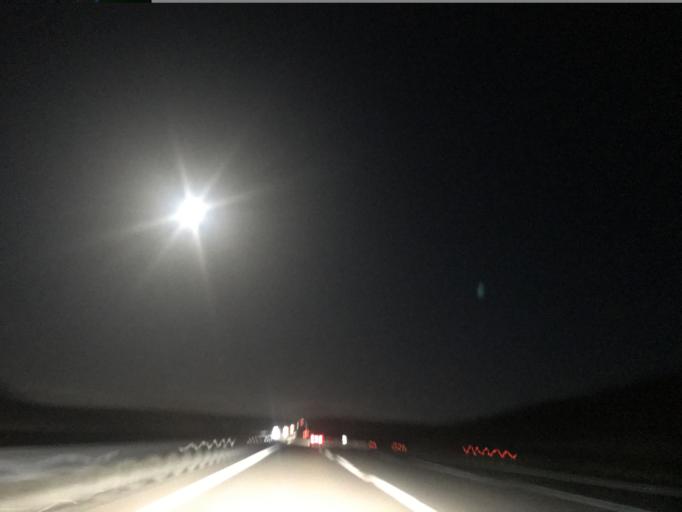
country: TR
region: Nigde
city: Ulukisla
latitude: 37.6398
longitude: 34.3863
